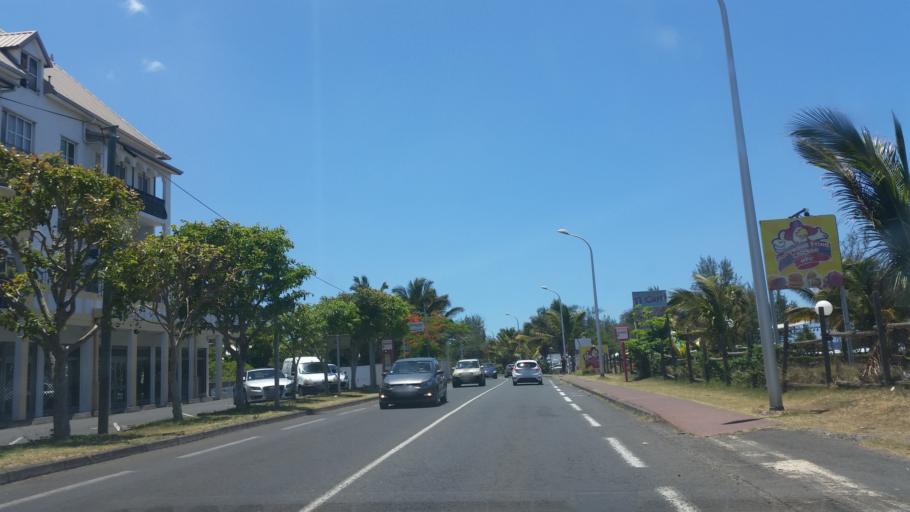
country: RE
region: Reunion
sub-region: Reunion
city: Saint-Pierre
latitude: -21.3372
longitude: 55.4575
